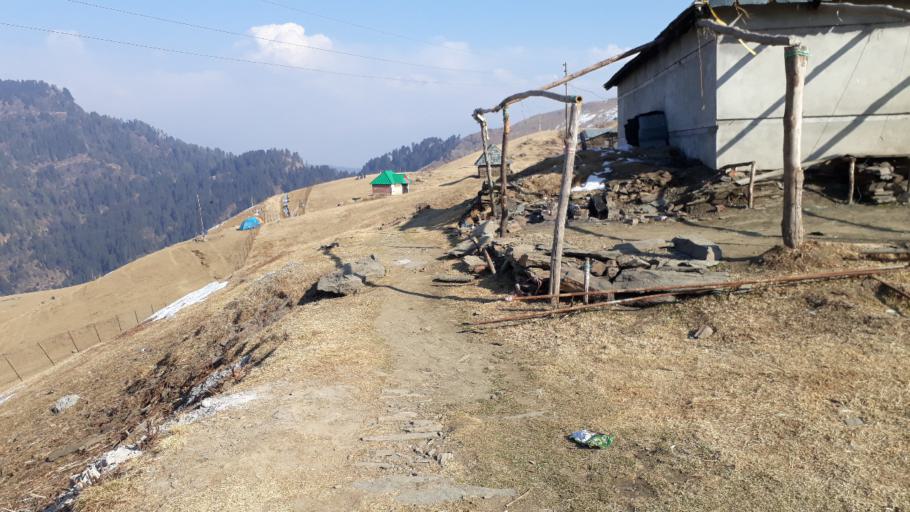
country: IN
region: Himachal Pradesh
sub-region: Mandi
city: Pandoh
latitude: 31.7559
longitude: 77.1002
